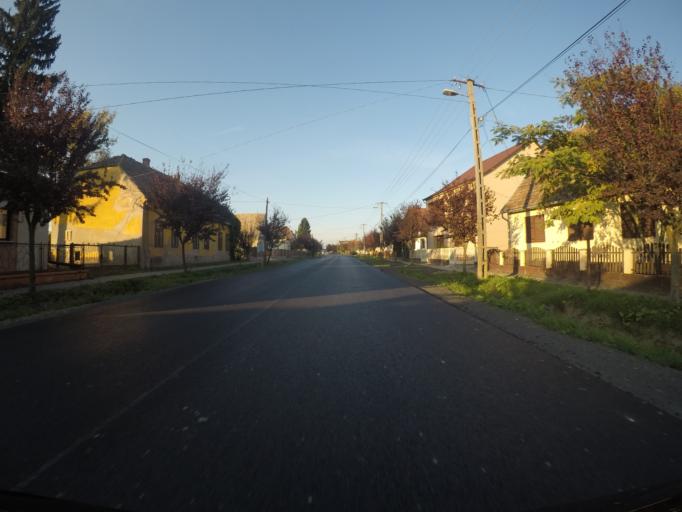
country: HU
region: Somogy
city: Barcs
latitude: 45.9830
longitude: 17.5901
